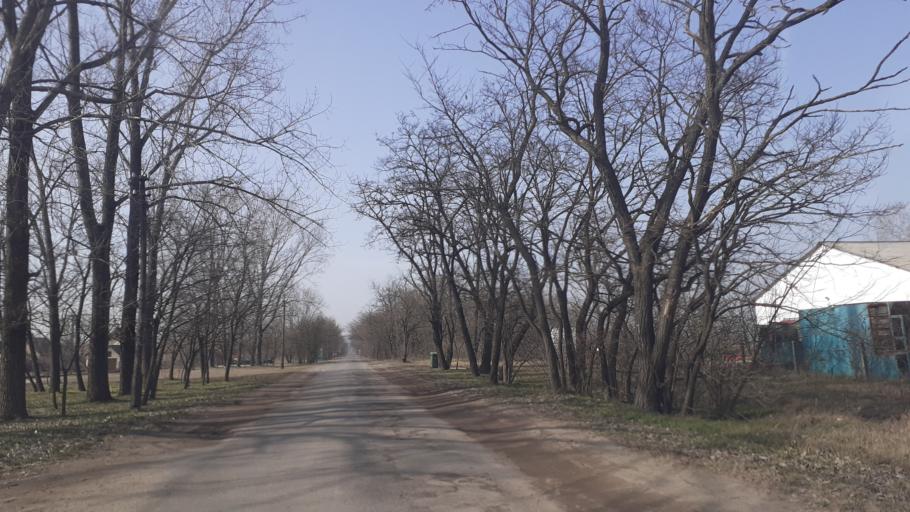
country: HU
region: Pest
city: Dabas
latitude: 47.0649
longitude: 19.2791
